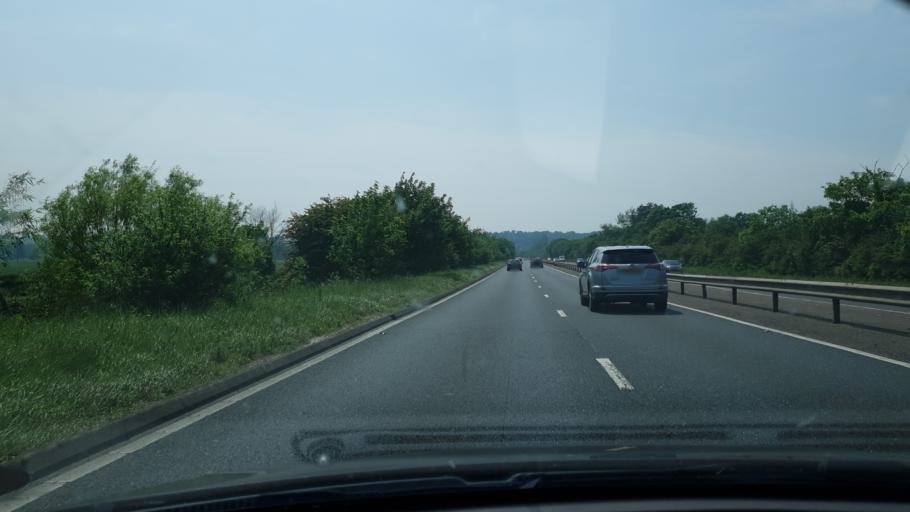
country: GB
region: England
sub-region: Suffolk
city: East Bergholt
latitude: 51.9706
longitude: 0.9817
